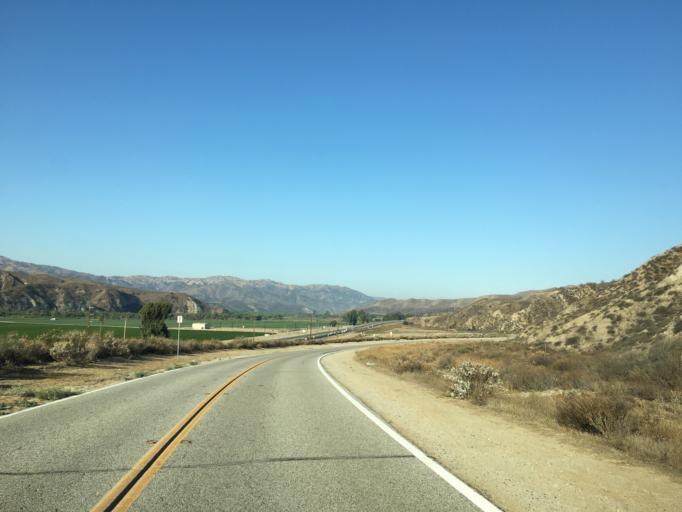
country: US
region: California
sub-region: Los Angeles County
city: Valencia
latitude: 34.4281
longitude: -118.6320
